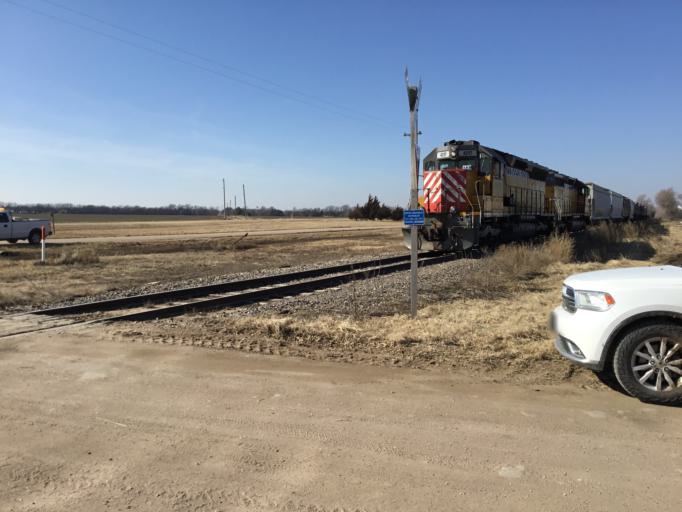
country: US
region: Kansas
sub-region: McPherson County
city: Moundridge
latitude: 38.1882
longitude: -97.5007
